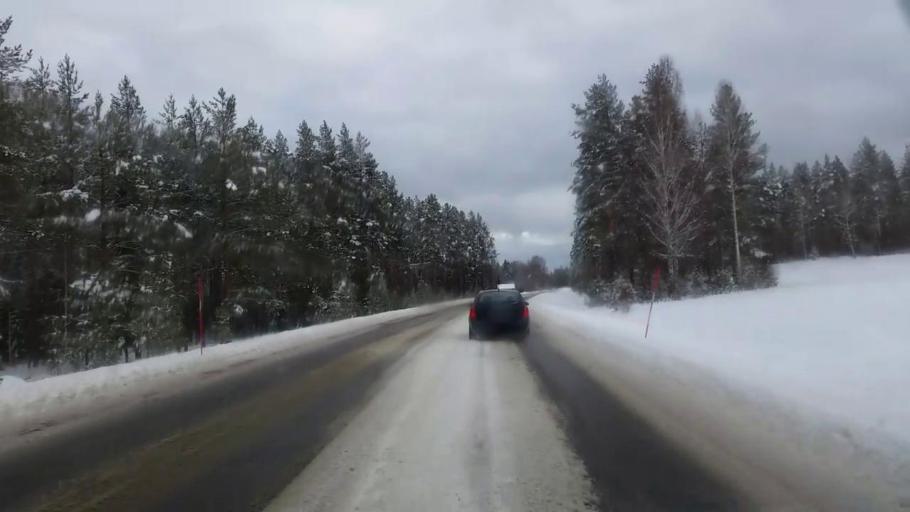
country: SE
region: Vaesternorrland
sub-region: Ange Kommun
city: Ange
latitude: 62.0537
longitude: 15.1396
